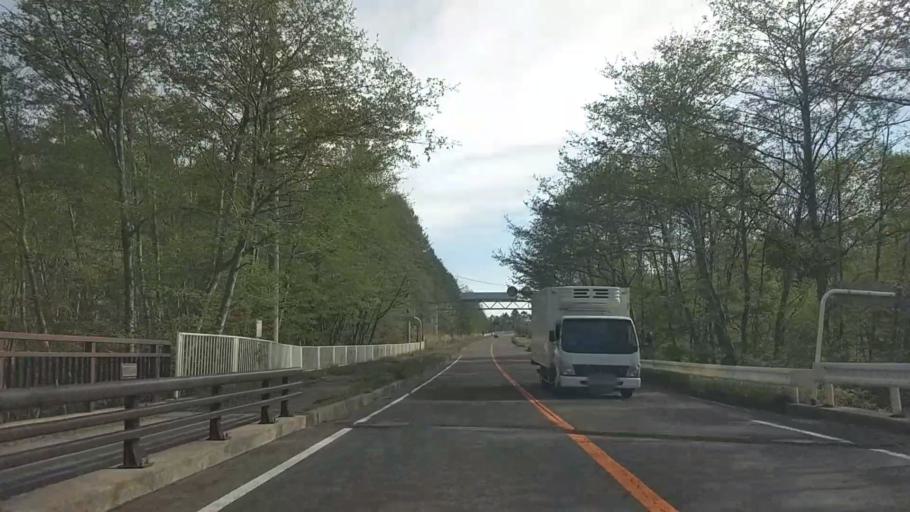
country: JP
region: Yamanashi
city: Nirasaki
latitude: 35.9401
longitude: 138.4494
